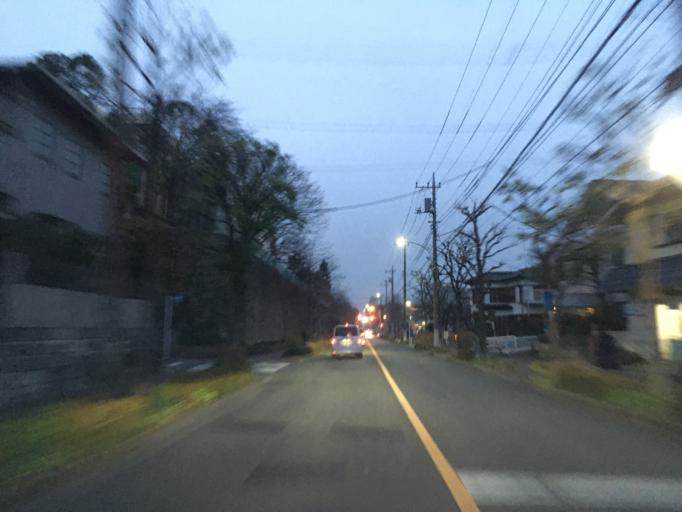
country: JP
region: Tokyo
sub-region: Machida-shi
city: Machida
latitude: 35.5179
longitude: 139.4784
